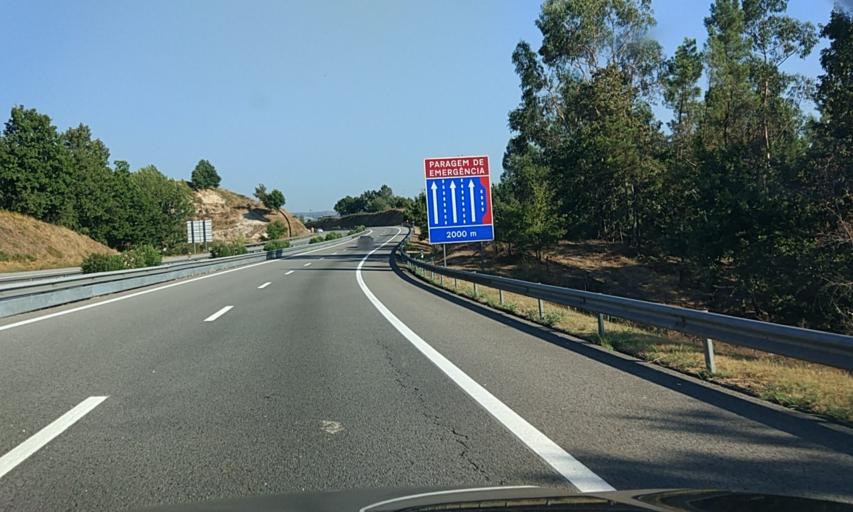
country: PT
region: Porto
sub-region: Marco de Canaveses
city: Marco de Canavezes
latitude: 41.2285
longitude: -8.1683
